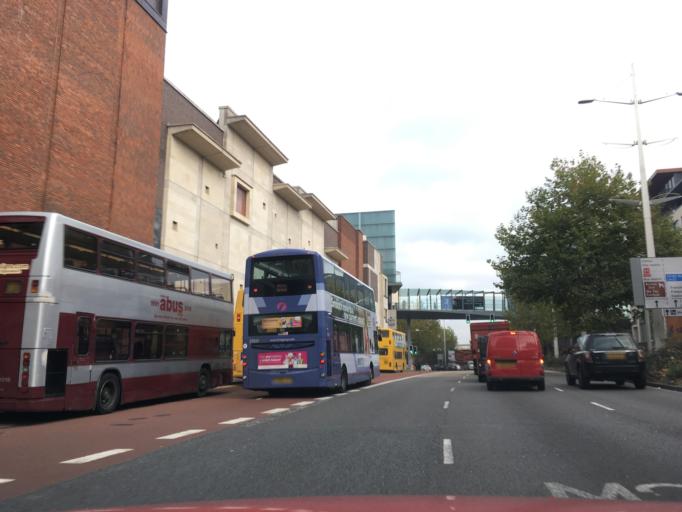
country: GB
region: England
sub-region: Bristol
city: Bristol
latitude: 51.4577
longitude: -2.5845
